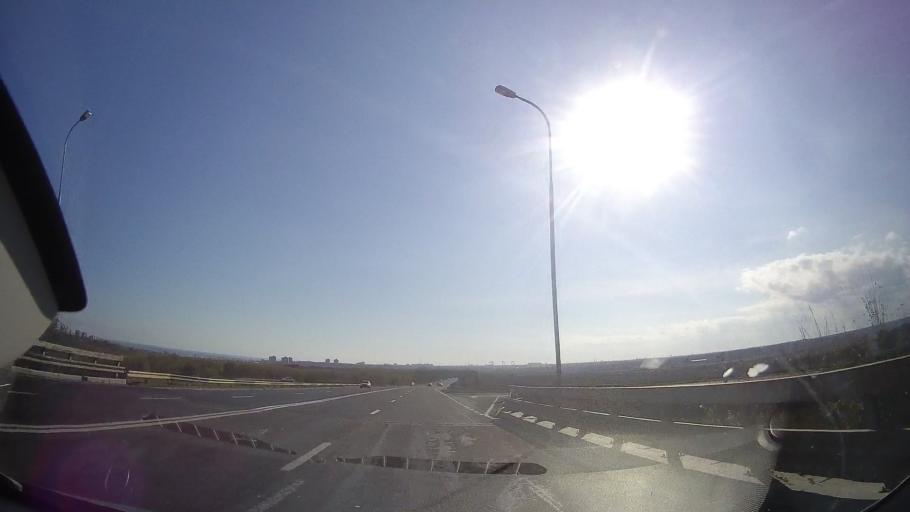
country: RO
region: Constanta
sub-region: Comuna Douazeci si Trei August
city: Dulcesti
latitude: 43.8569
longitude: 28.5759
